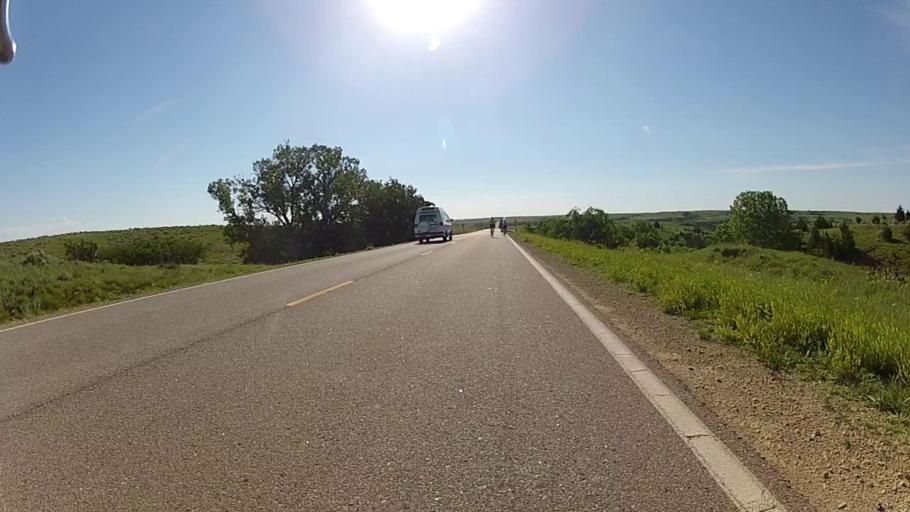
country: US
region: Kansas
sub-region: Barber County
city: Medicine Lodge
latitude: 37.2816
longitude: -98.8865
